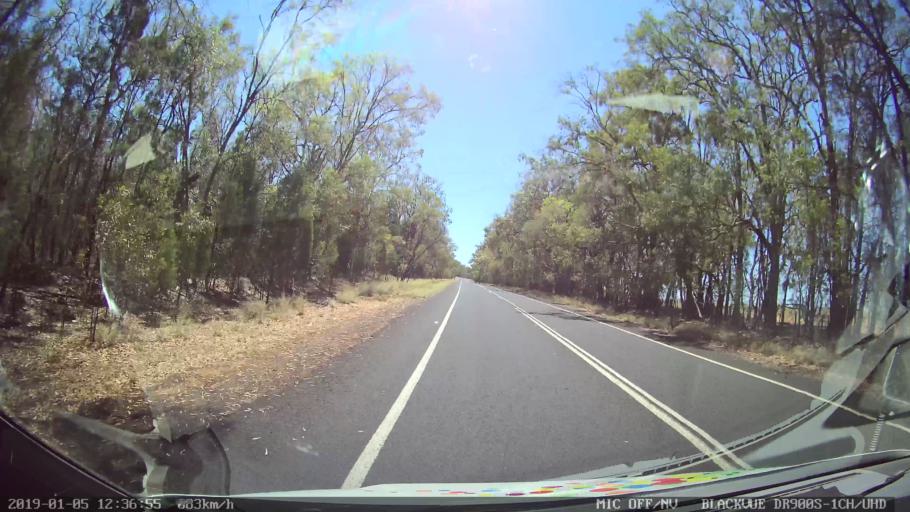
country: AU
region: New South Wales
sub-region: Warrumbungle Shire
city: Coonabarabran
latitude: -31.2059
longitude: 149.4475
